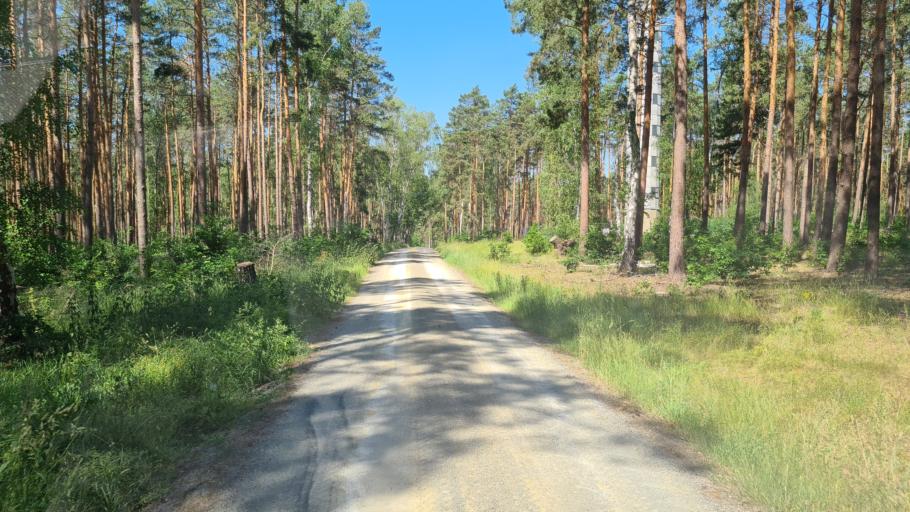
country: DE
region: Brandenburg
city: Lebusa
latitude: 51.7762
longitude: 13.3931
